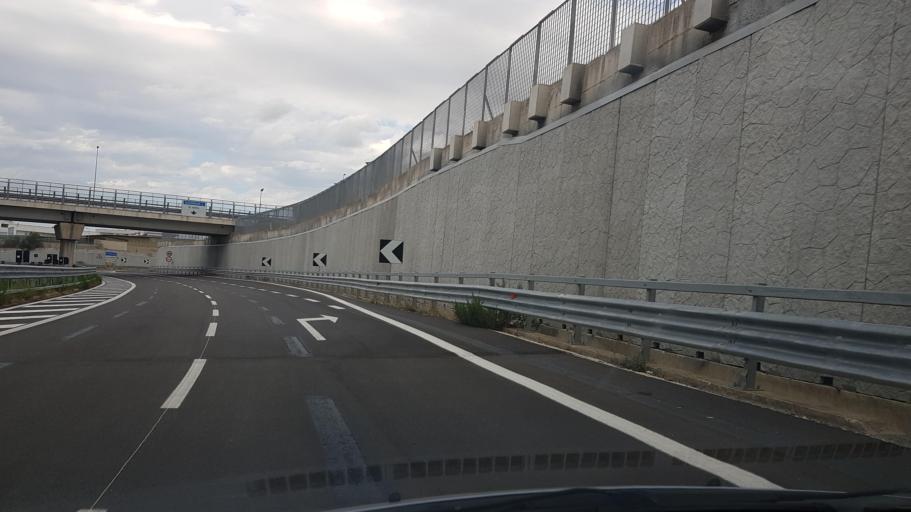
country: IT
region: Apulia
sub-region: Provincia di Taranto
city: Taranto
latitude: 40.4616
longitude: 17.2891
